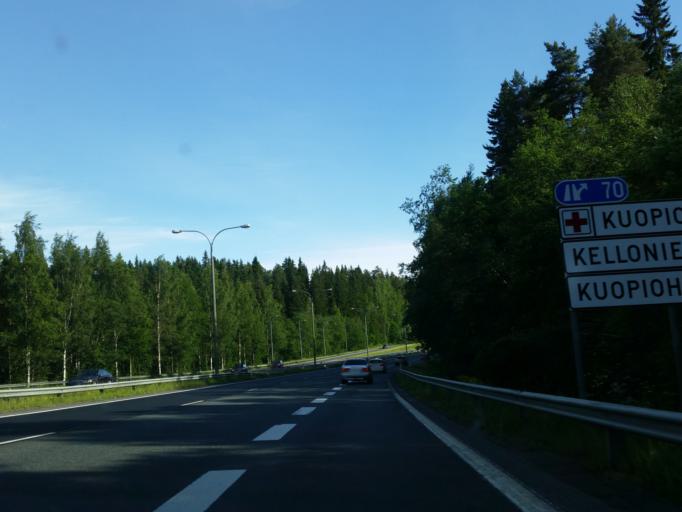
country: FI
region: Northern Savo
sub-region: Kuopio
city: Kuopio
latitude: 62.9108
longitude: 27.6863
